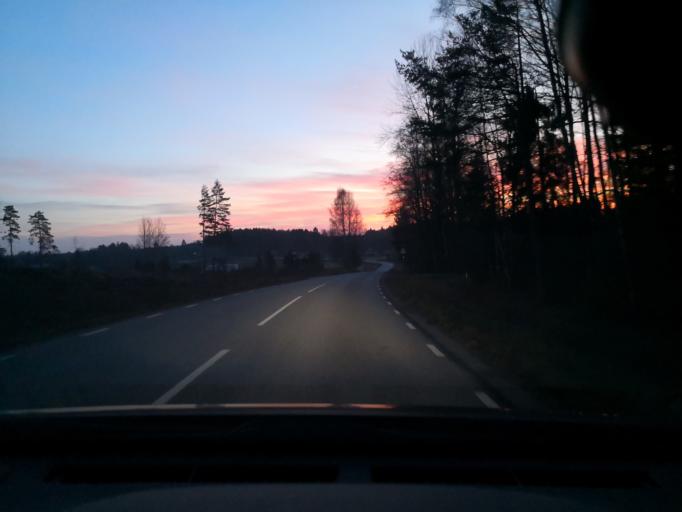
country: SE
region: OErebro
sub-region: Lindesbergs Kommun
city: Frovi
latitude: 59.3732
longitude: 15.4343
